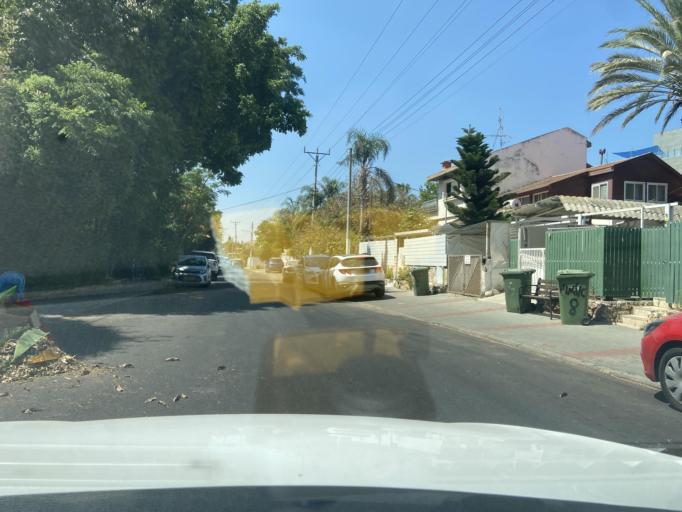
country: IL
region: Tel Aviv
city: Or Yehuda
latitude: 32.0322
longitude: 34.8692
